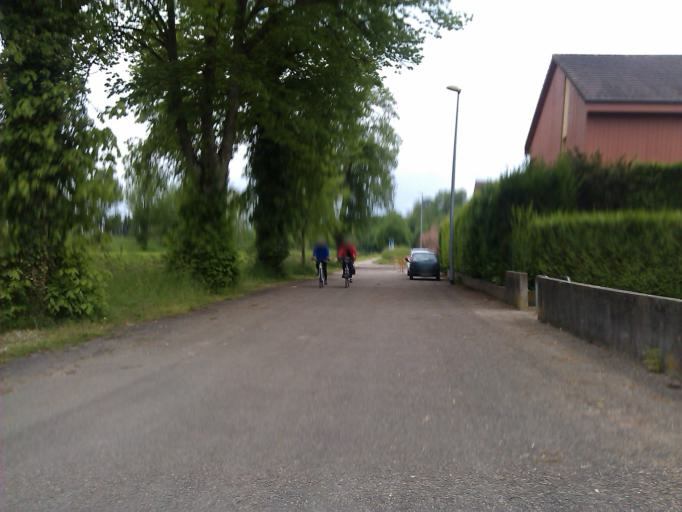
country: FR
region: Franche-Comte
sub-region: Departement du Jura
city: Foucherans
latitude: 47.0791
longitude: 5.4775
